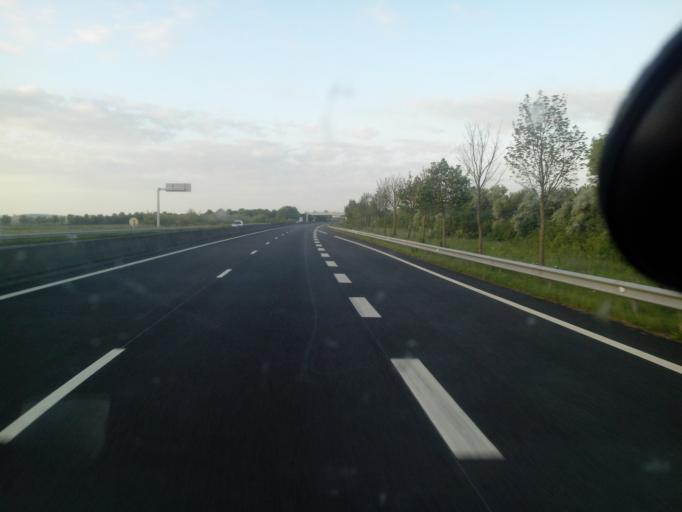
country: FR
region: Picardie
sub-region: Departement de la Somme
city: Bouttencourt
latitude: 49.9650
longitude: 1.6593
